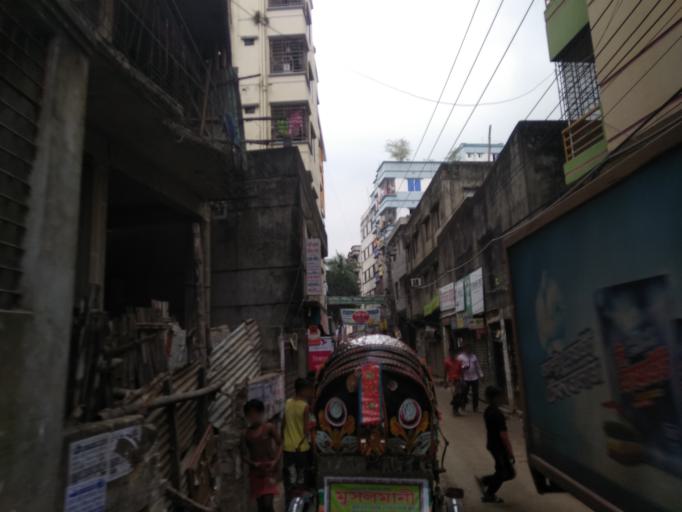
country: BD
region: Dhaka
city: Paltan
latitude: 23.7843
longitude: 90.4269
